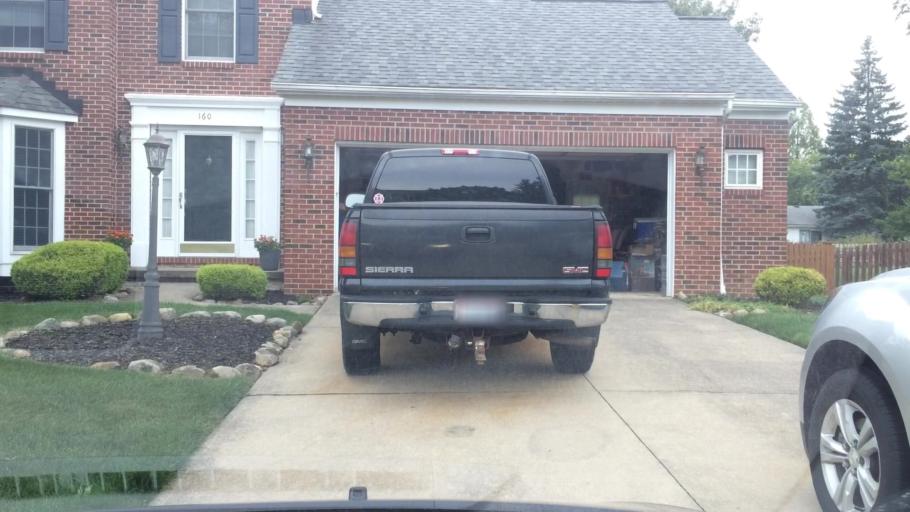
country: US
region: Ohio
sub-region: Medina County
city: Brunswick
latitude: 41.2715
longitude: -81.8175
